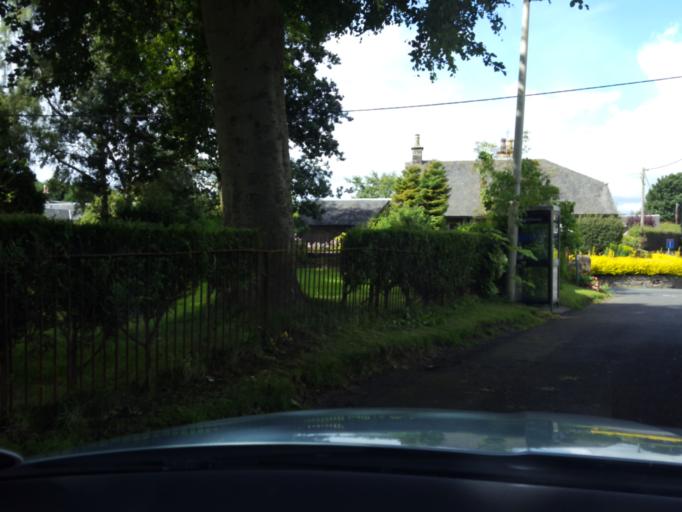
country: GB
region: Scotland
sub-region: West Lothian
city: Linlithgow
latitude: 56.0073
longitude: -3.5745
